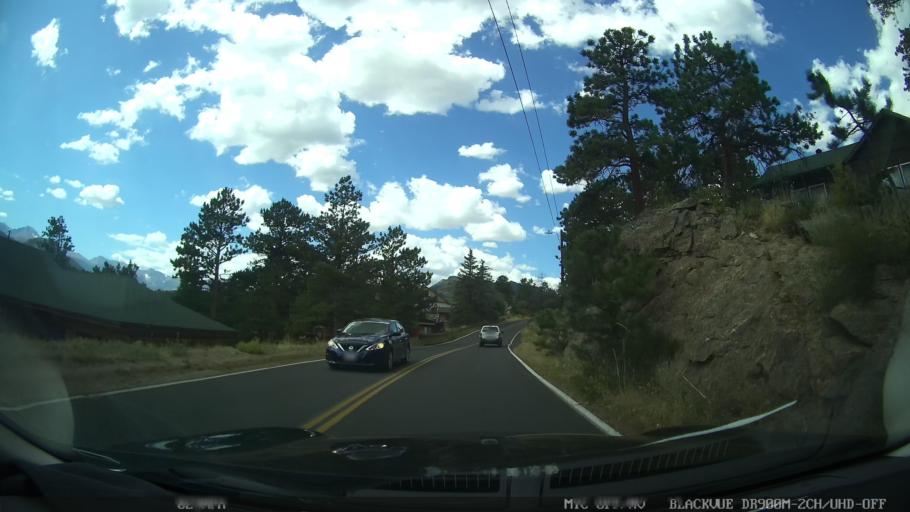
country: US
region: Colorado
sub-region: Larimer County
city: Estes Park
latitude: 40.3783
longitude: -105.5257
